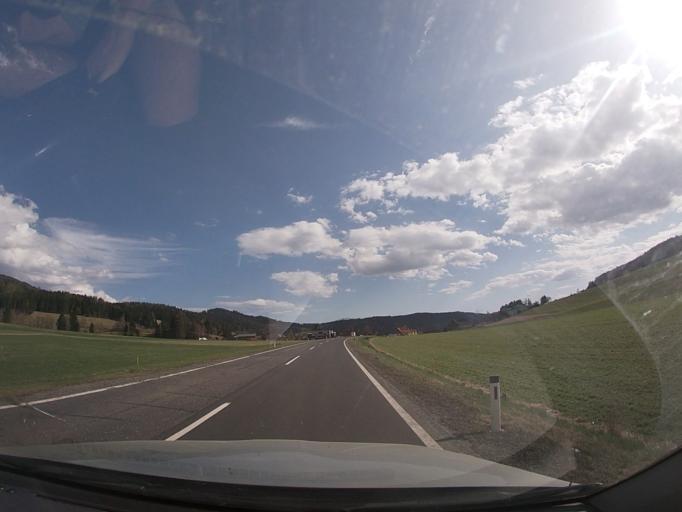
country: AT
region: Styria
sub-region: Politischer Bezirk Murau
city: Perchau am Sattel
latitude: 47.1120
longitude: 14.4576
